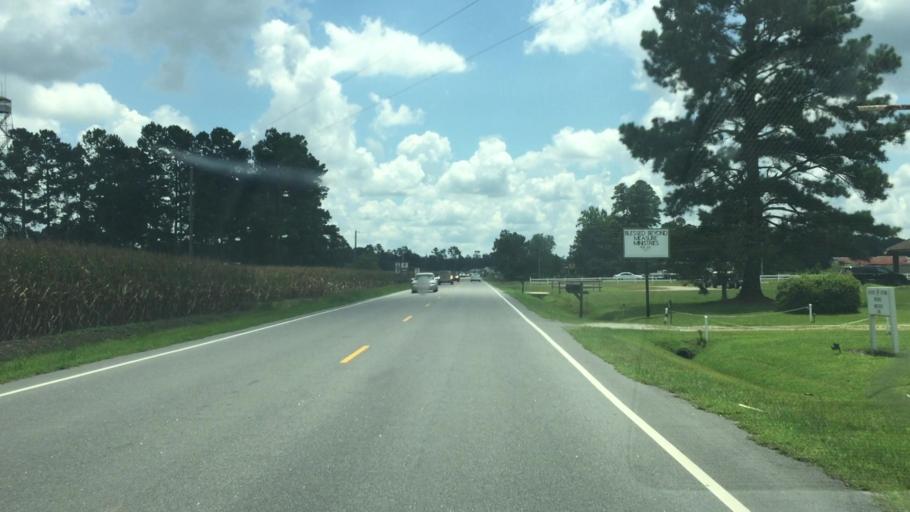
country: US
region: North Carolina
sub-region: Columbus County
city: Chadbourn
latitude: 34.2801
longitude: -78.8167
